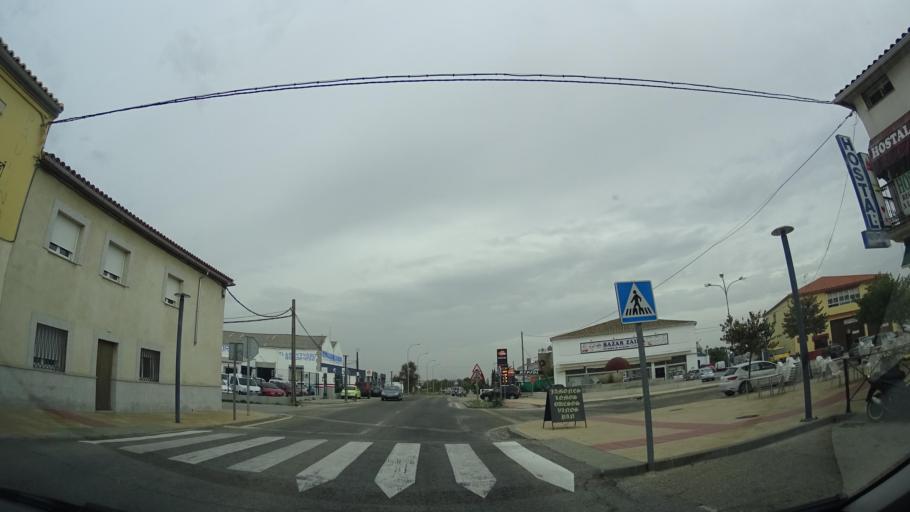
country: ES
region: Extremadura
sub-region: Provincia de Caceres
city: Trujillo
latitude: 39.4597
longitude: -5.8720
